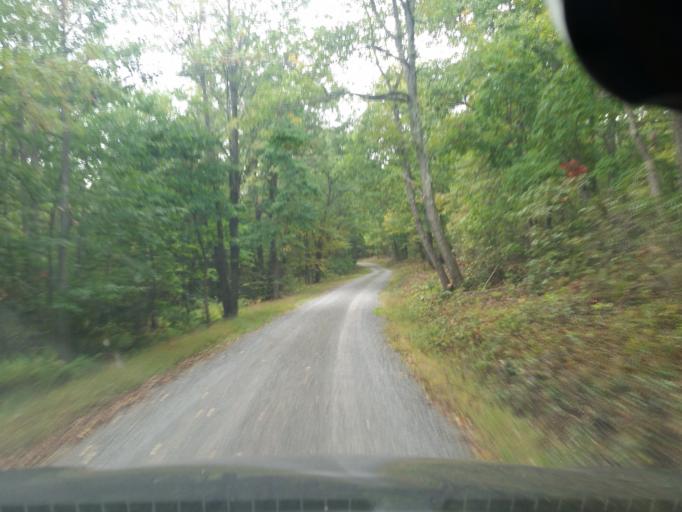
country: US
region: Pennsylvania
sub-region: Lycoming County
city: Jersey Shore
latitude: 41.0831
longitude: -77.2064
